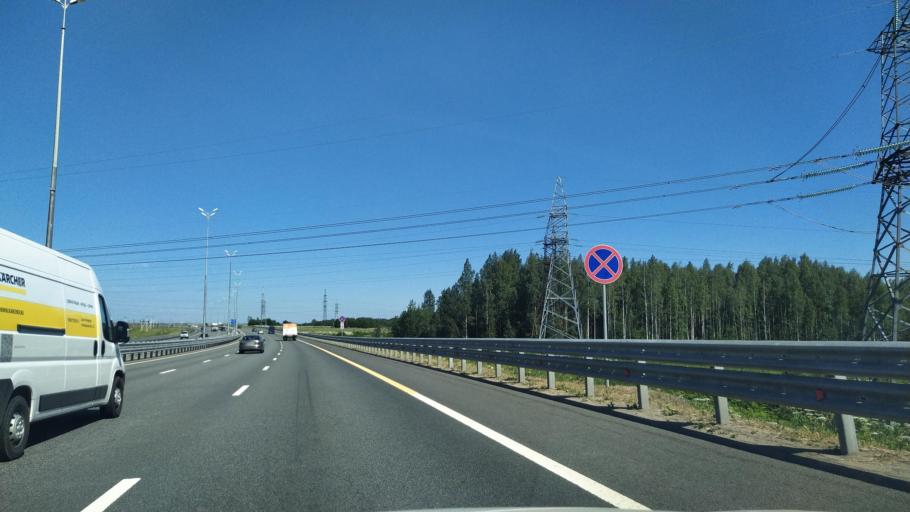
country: RU
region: Leningrad
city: Gatchina
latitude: 59.5281
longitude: 30.1318
